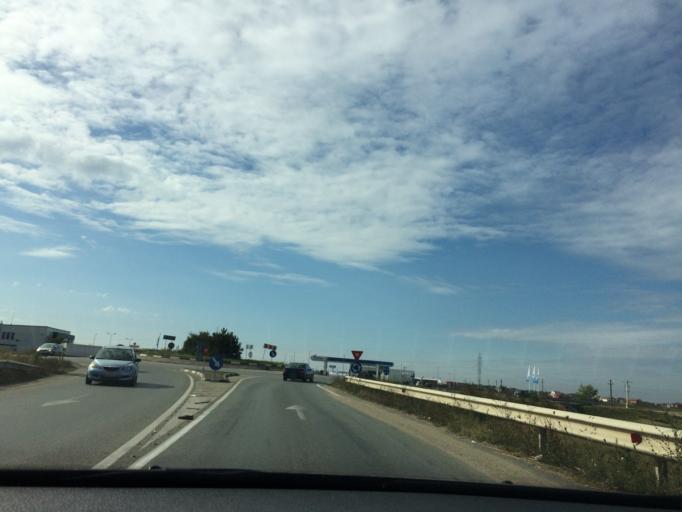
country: RO
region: Timis
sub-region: Comuna Dumbravita
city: Dumbravita
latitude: 45.8146
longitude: 21.2632
